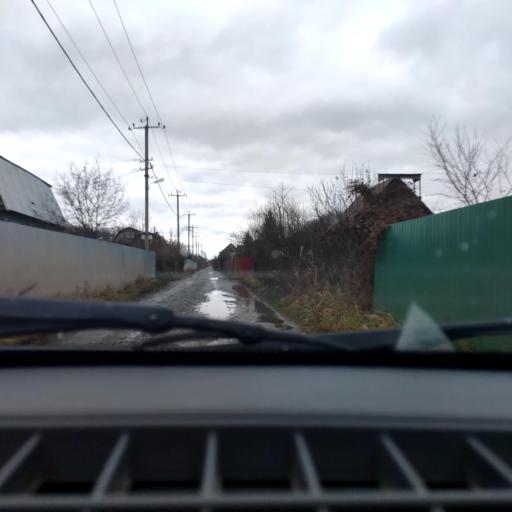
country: RU
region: Bashkortostan
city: Avdon
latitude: 54.6251
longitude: 55.7223
